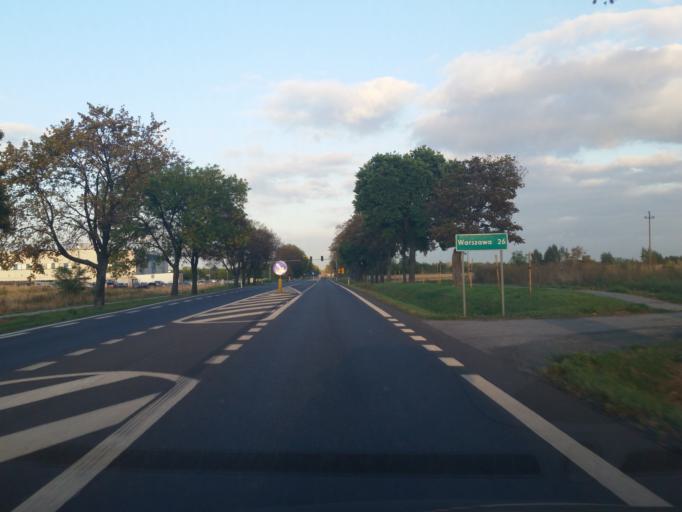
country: PL
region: Masovian Voivodeship
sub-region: Powiat warszawski zachodni
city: Jozefow
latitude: 52.2091
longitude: 20.6660
